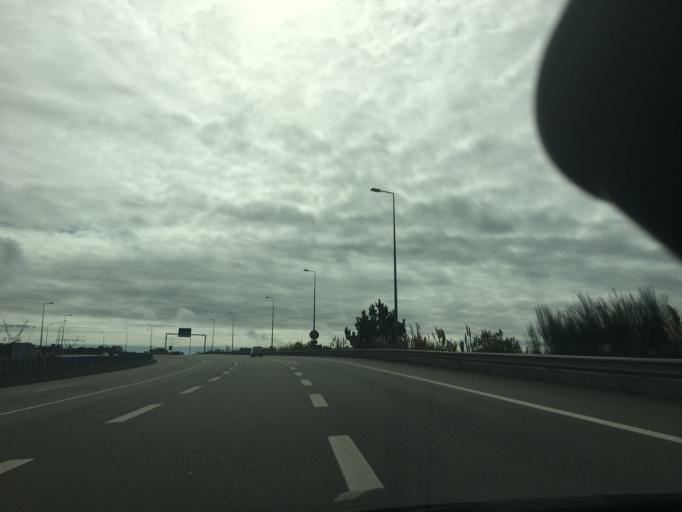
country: PT
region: Porto
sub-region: Matosinhos
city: Guifoes
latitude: 41.2064
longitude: -8.6519
